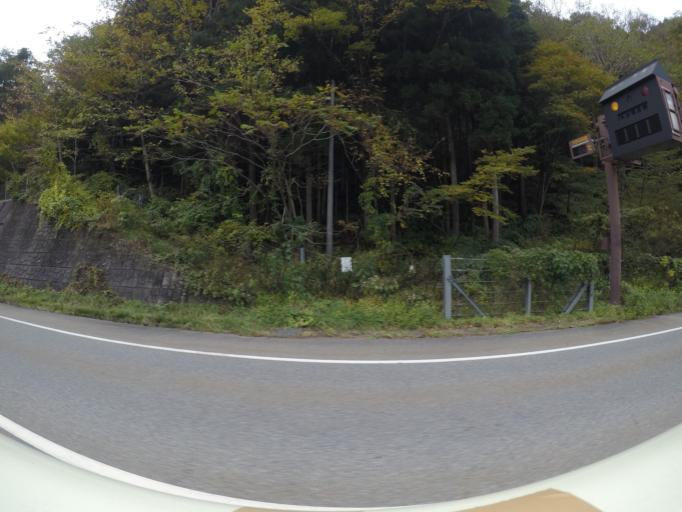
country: JP
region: Nagano
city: Ina
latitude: 35.9104
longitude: 137.8140
